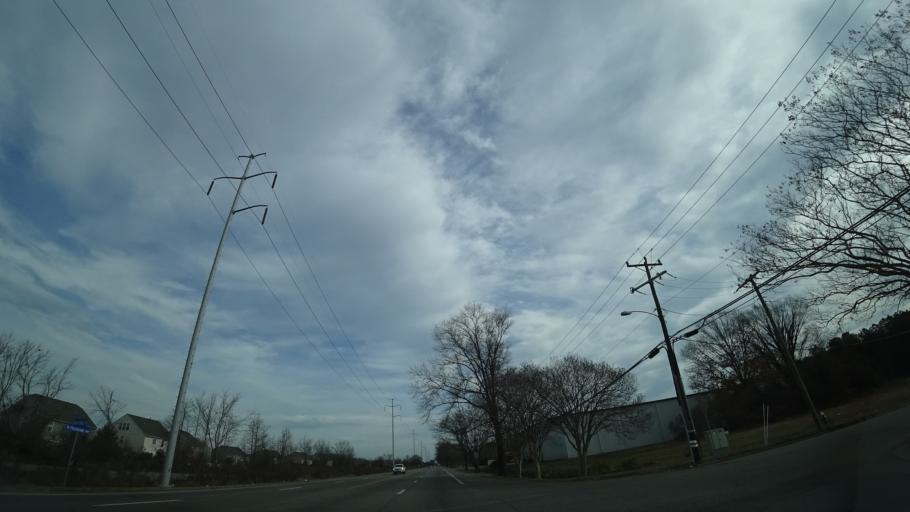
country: US
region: Virginia
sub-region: City of Hampton
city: Hampton
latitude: 37.0198
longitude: -76.3746
